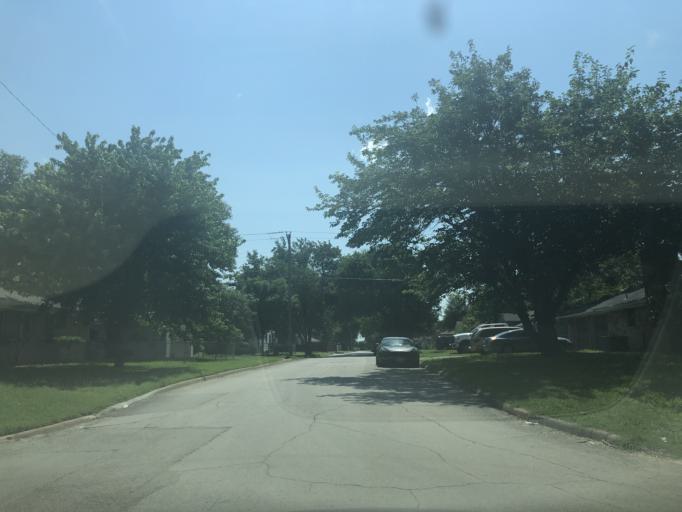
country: US
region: Texas
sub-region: Dallas County
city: Grand Prairie
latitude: 32.7309
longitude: -97.0092
